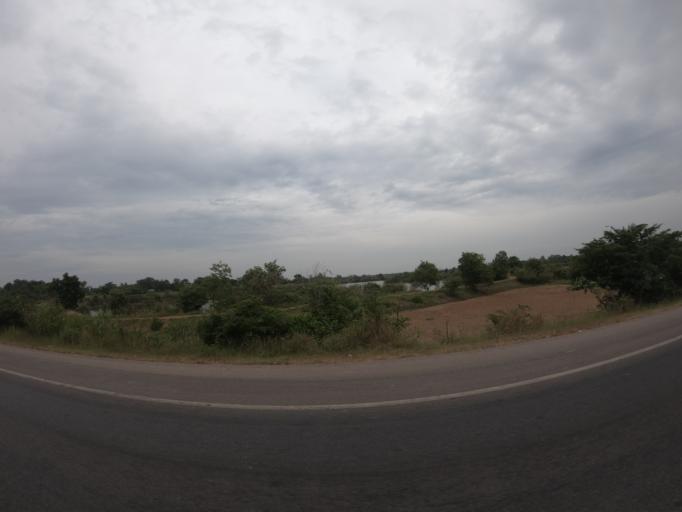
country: TH
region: Roi Et
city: Chiang Khwan
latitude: 16.1213
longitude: 103.8458
